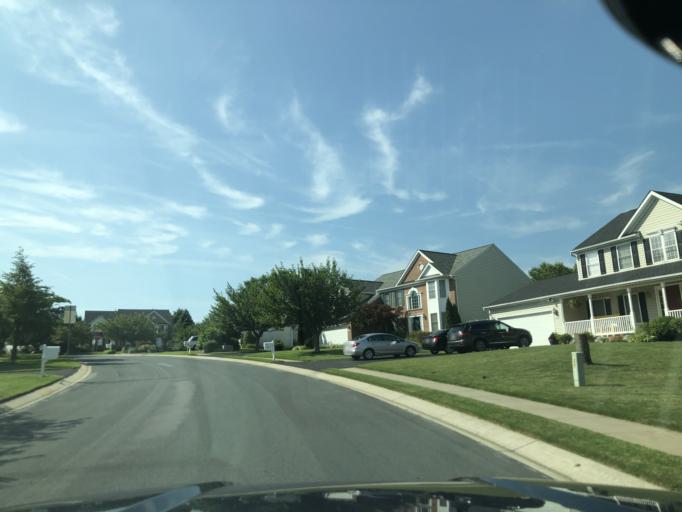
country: US
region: Maryland
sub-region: Carroll County
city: Eldersburg
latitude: 39.4124
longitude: -76.9669
